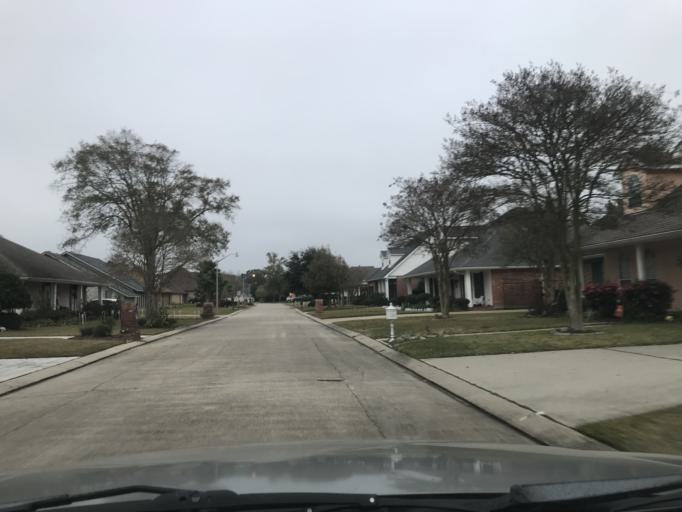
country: US
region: Louisiana
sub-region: Jefferson Parish
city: Woodmere
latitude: 29.8701
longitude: -90.0922
